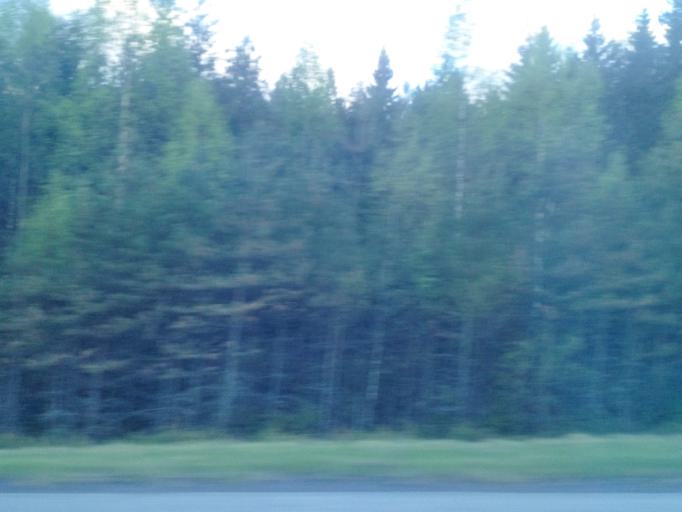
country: FI
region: Haeme
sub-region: Haemeenlinna
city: Kalvola
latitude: 61.1163
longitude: 24.1313
